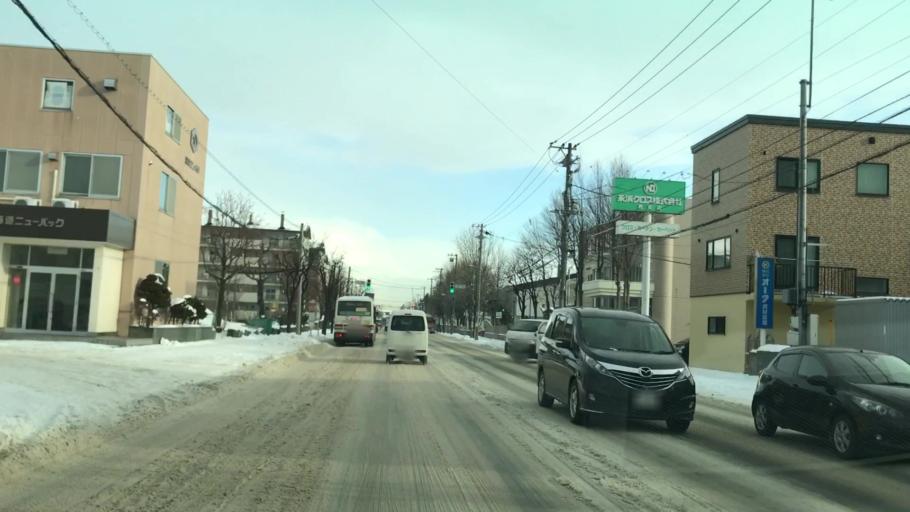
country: JP
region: Hokkaido
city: Sapporo
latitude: 43.0949
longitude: 141.3046
